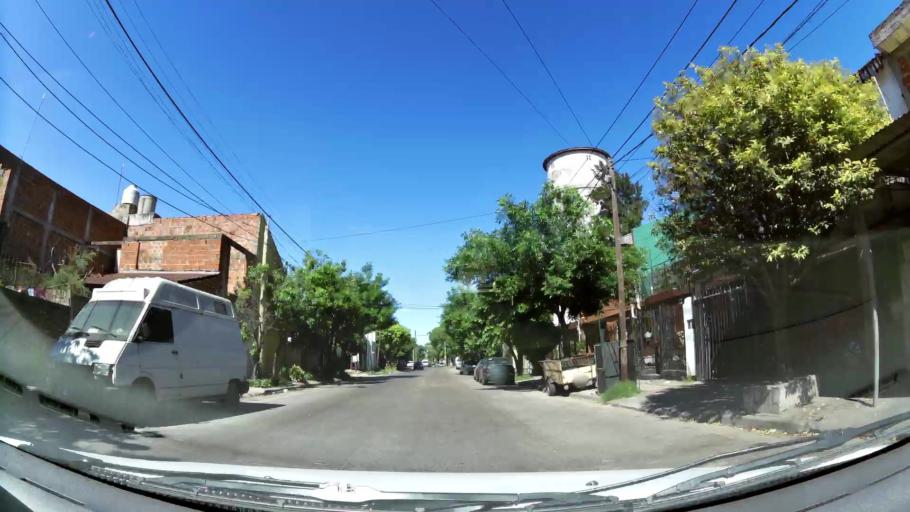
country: AR
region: Buenos Aires
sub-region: Partido de General San Martin
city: General San Martin
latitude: -34.5510
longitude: -58.5257
